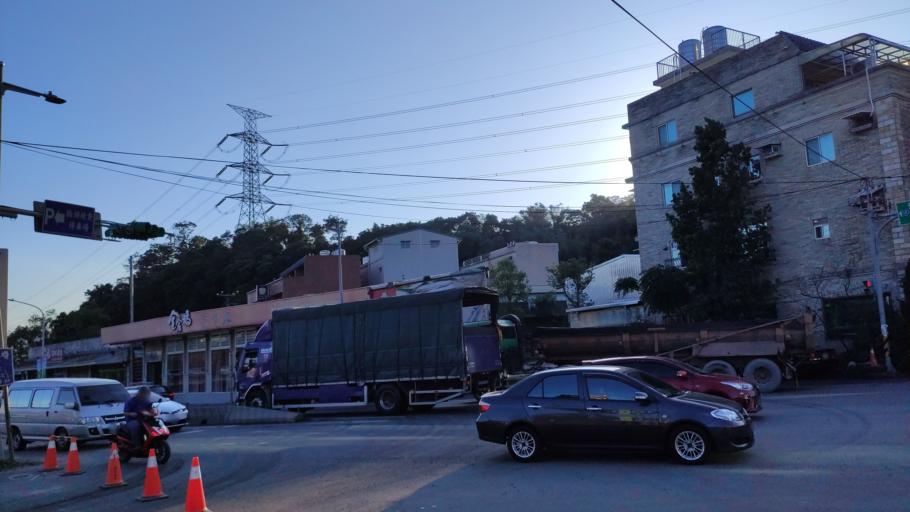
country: TW
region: Taiwan
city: Daxi
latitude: 24.8856
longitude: 121.2803
